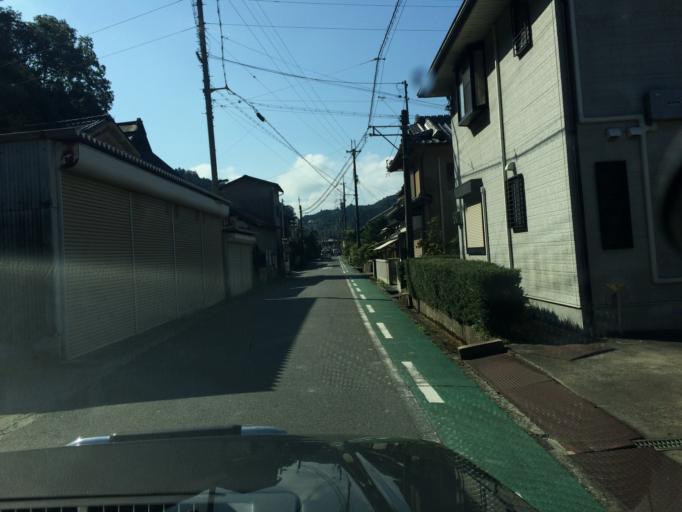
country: JP
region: Nara
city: Nara-shi
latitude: 34.7365
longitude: 135.9522
